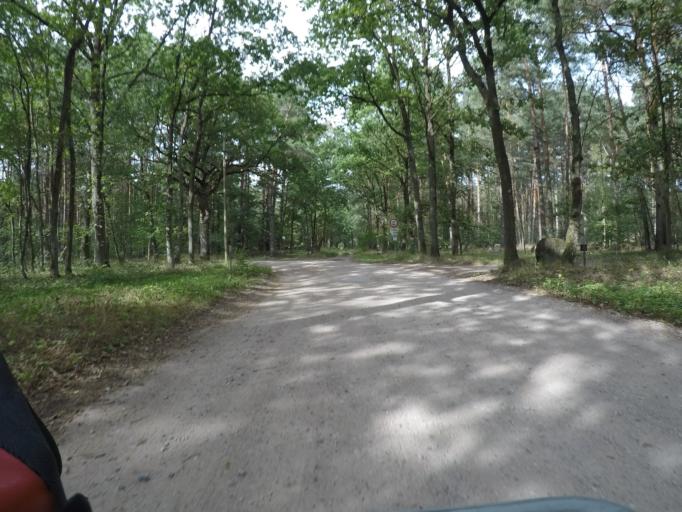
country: DE
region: Lower Saxony
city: Wittorf
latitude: 53.3287
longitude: 10.3989
